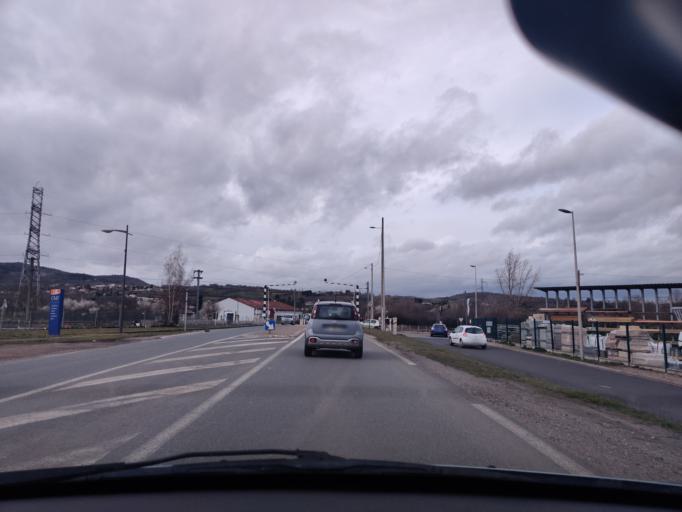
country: FR
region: Auvergne
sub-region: Departement du Puy-de-Dome
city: Mozac
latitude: 45.8912
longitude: 3.0736
